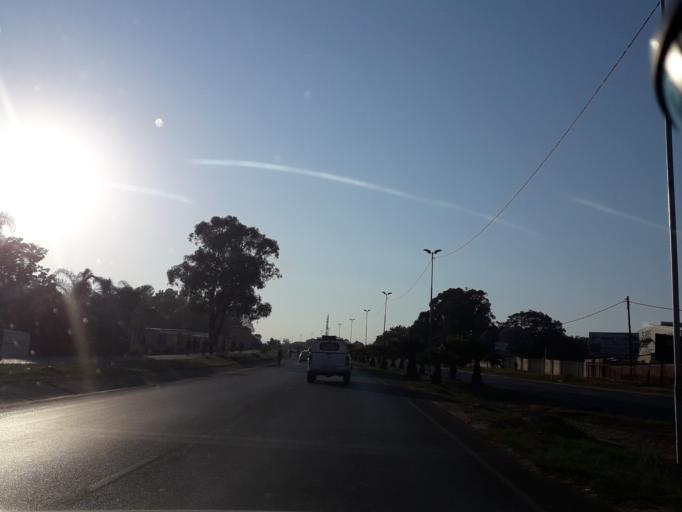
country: ZA
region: Gauteng
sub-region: West Rand District Municipality
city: Muldersdriseloop
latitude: -26.0717
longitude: 27.9146
